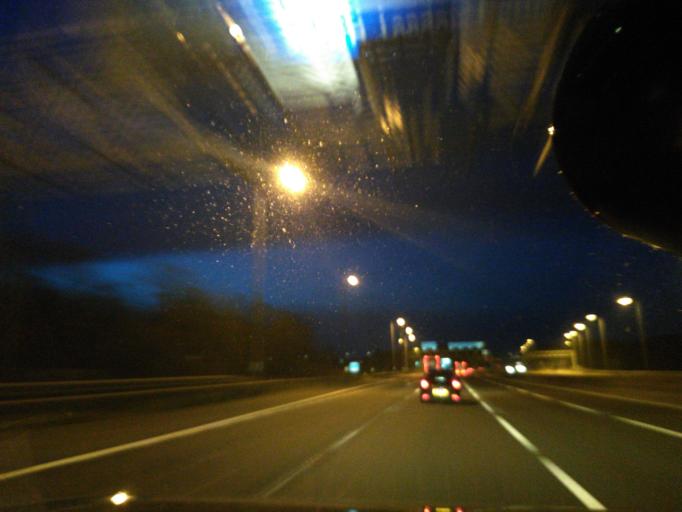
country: GB
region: England
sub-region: Nottinghamshire
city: Kirkby in Ashfield
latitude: 53.0677
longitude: -1.2741
